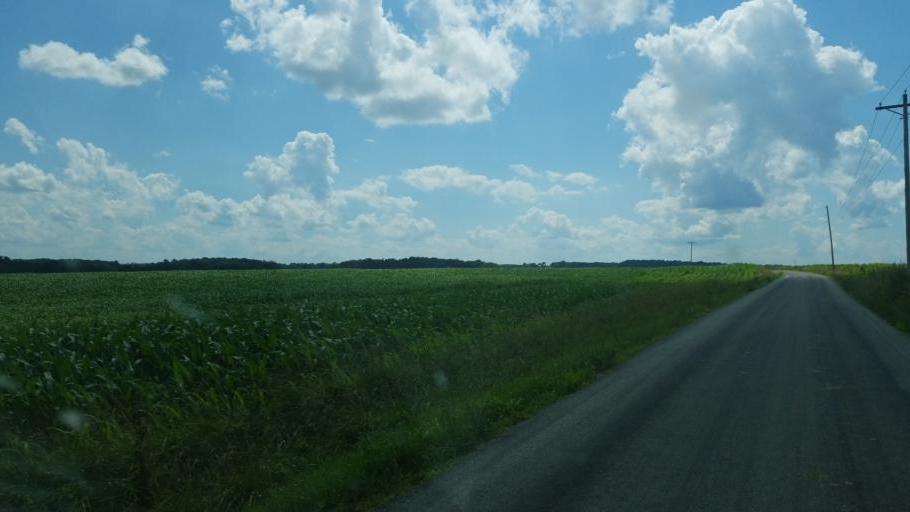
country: US
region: Ohio
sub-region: Highland County
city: Greenfield
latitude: 39.2477
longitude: -83.4224
